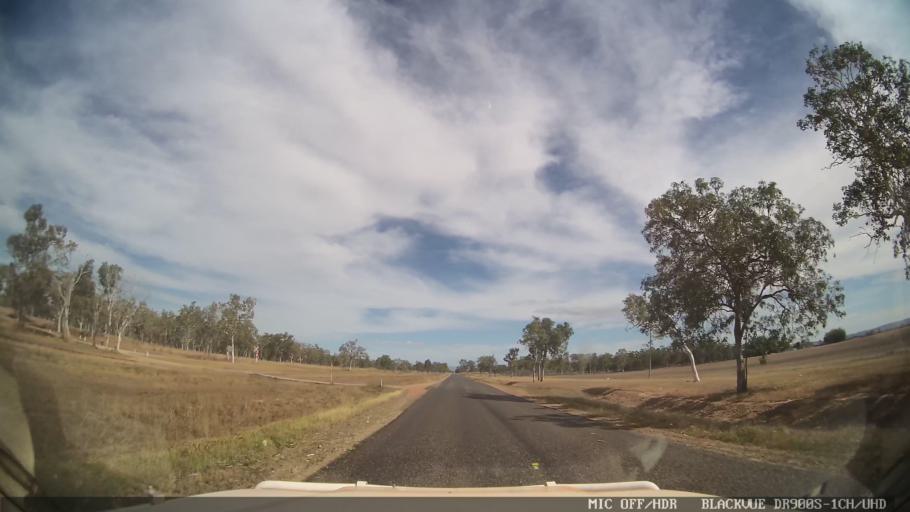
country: AU
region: Queensland
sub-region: Tablelands
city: Mareeba
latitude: -16.9325
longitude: 145.4178
